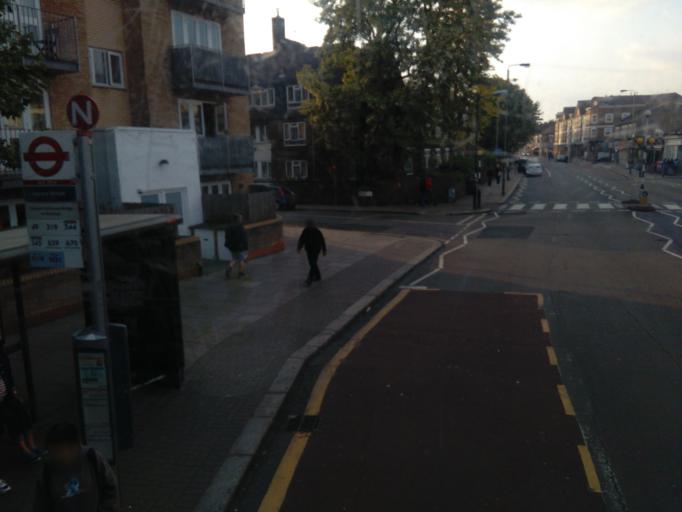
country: GB
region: England
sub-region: Greater London
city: Battersea
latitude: 51.4672
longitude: -0.1705
